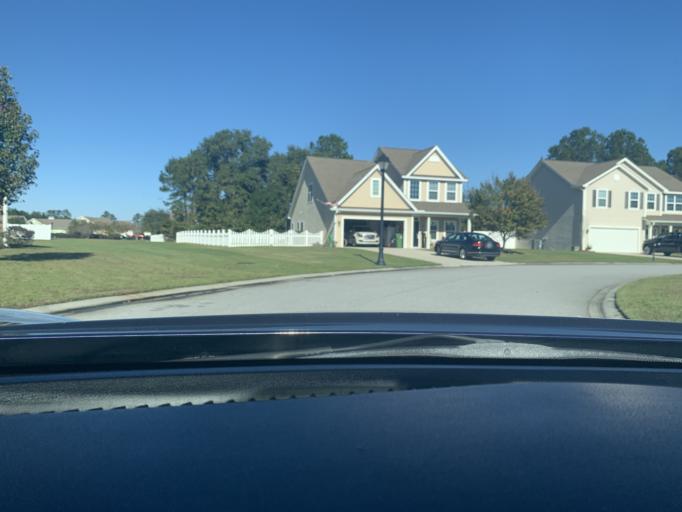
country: US
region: Georgia
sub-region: Chatham County
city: Pooler
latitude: 32.0718
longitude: -81.2701
